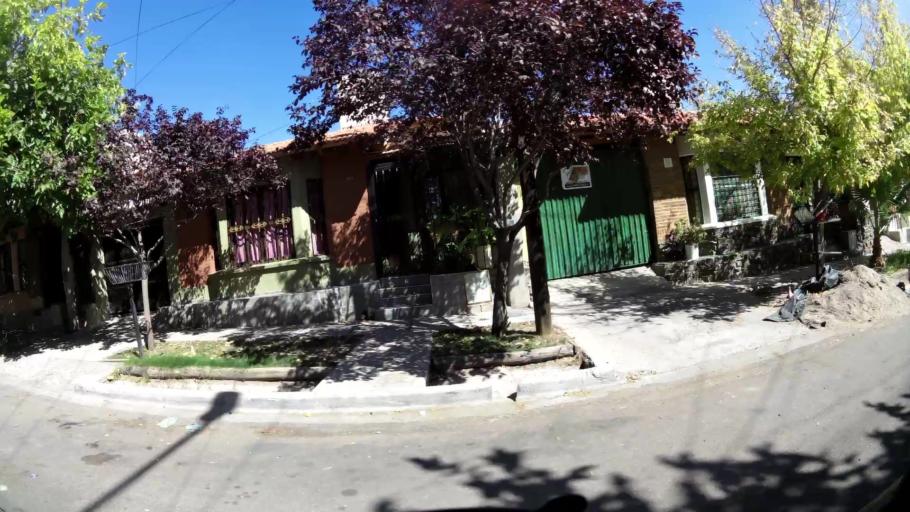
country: AR
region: Mendoza
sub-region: Departamento de Godoy Cruz
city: Godoy Cruz
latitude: -32.9108
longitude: -68.8799
